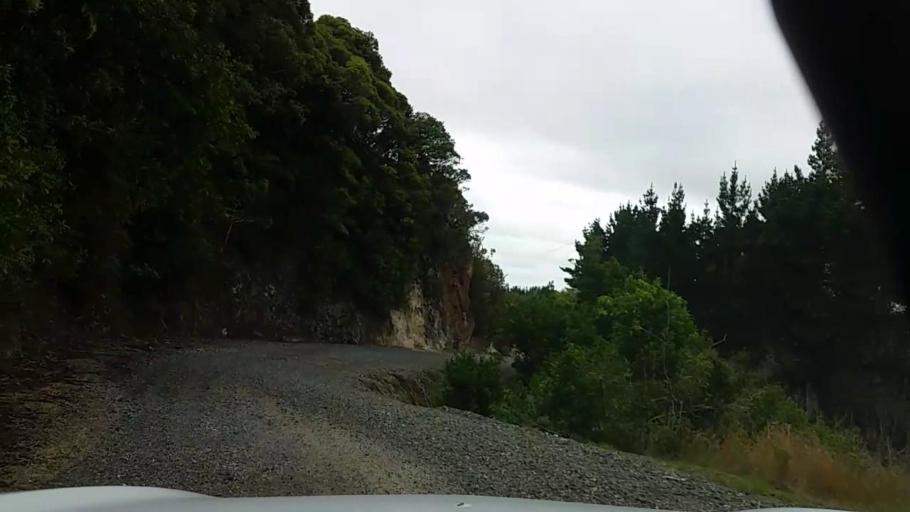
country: NZ
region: Northland
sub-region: Far North District
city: Kawakawa
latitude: -35.4612
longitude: 174.2632
